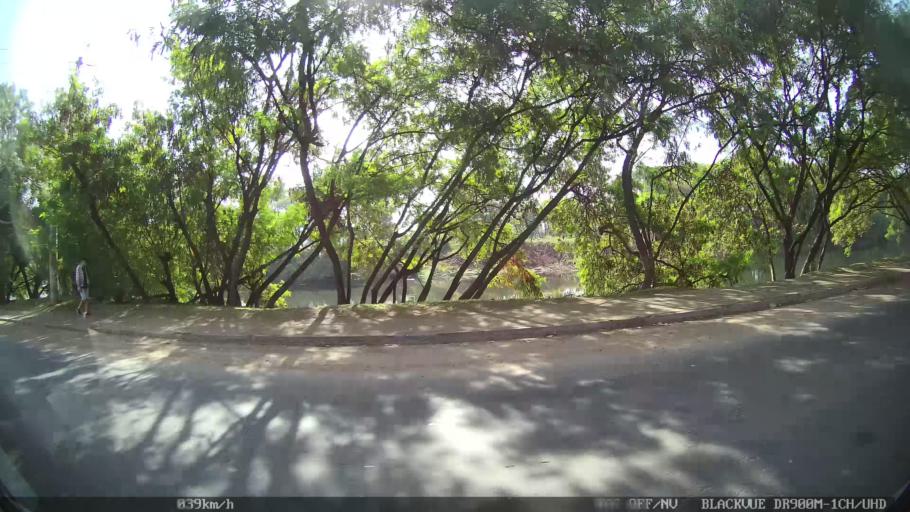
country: BR
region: Sao Paulo
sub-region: Piracicaba
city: Piracicaba
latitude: -22.7194
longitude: -47.6754
